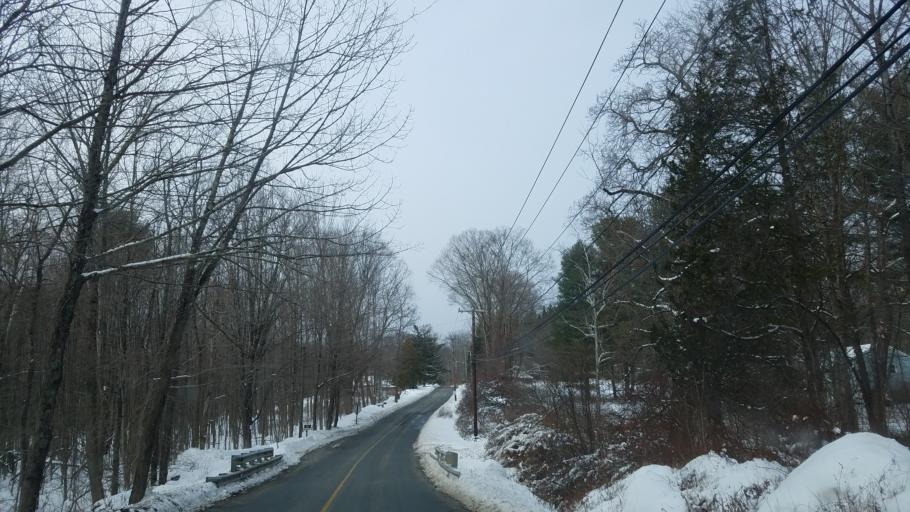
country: US
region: Connecticut
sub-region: Litchfield County
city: New Hartford Center
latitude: 41.8712
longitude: -73.0296
